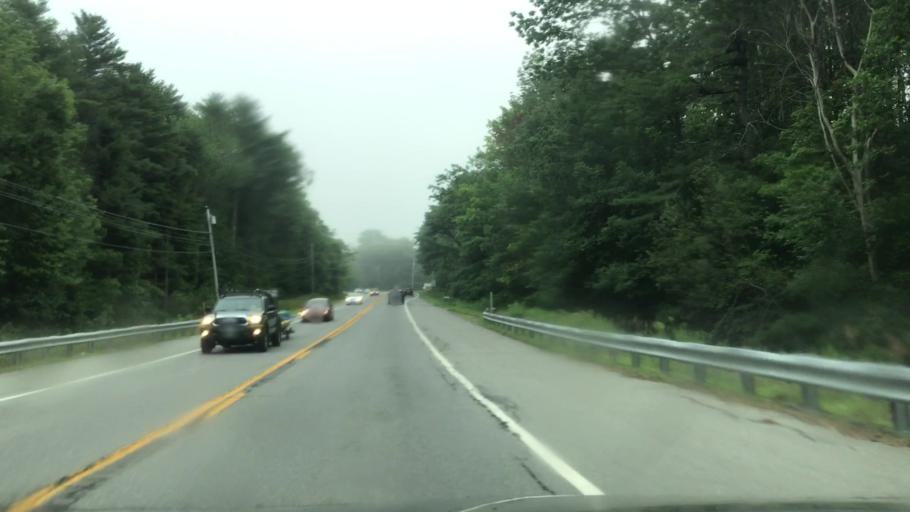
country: US
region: Maine
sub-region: Lincoln County
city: Waldoboro
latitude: 44.1020
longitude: -69.4256
